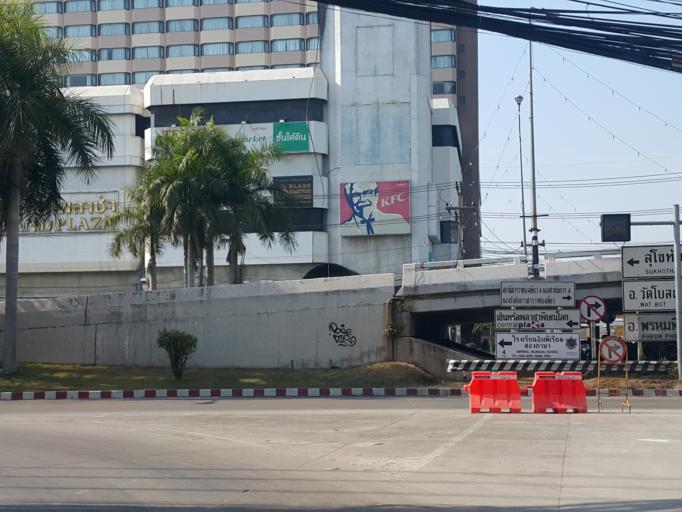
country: TH
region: Phitsanulok
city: Phitsanulok
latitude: 16.8206
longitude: 100.2651
